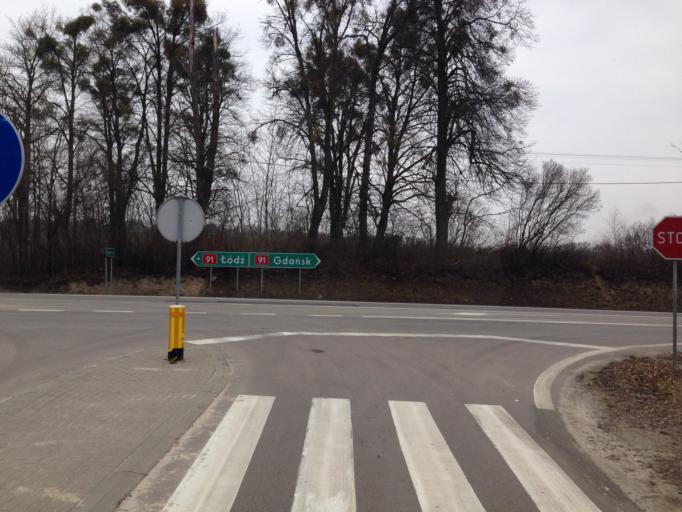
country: PL
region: Pomeranian Voivodeship
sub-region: Powiat starogardzki
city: Smetowo Graniczne
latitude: 53.7491
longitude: 18.7551
